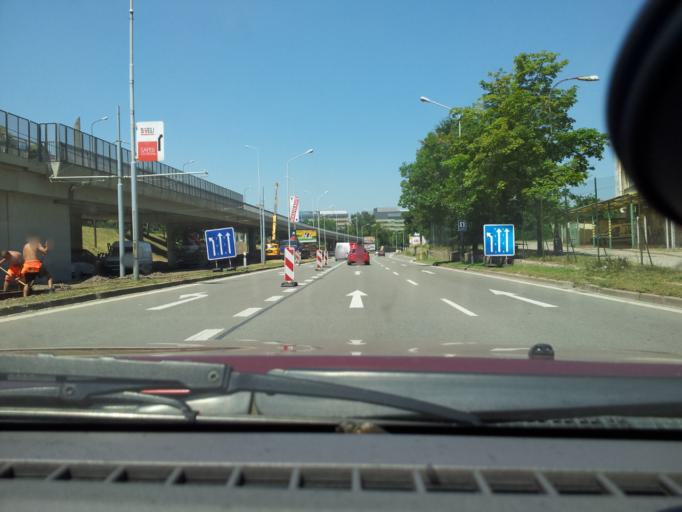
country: CZ
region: South Moravian
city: Moravany
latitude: 49.1665
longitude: 16.5990
